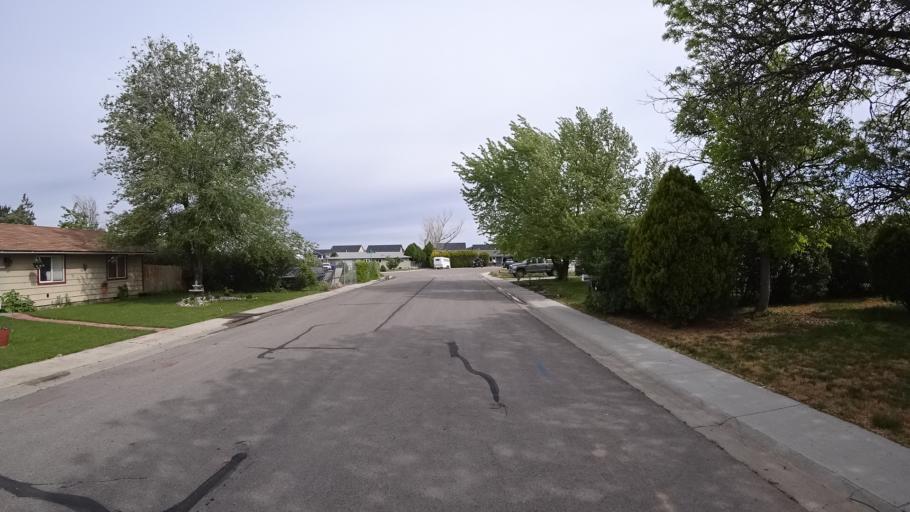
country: US
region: Idaho
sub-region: Ada County
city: Garden City
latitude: 43.5382
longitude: -116.3052
